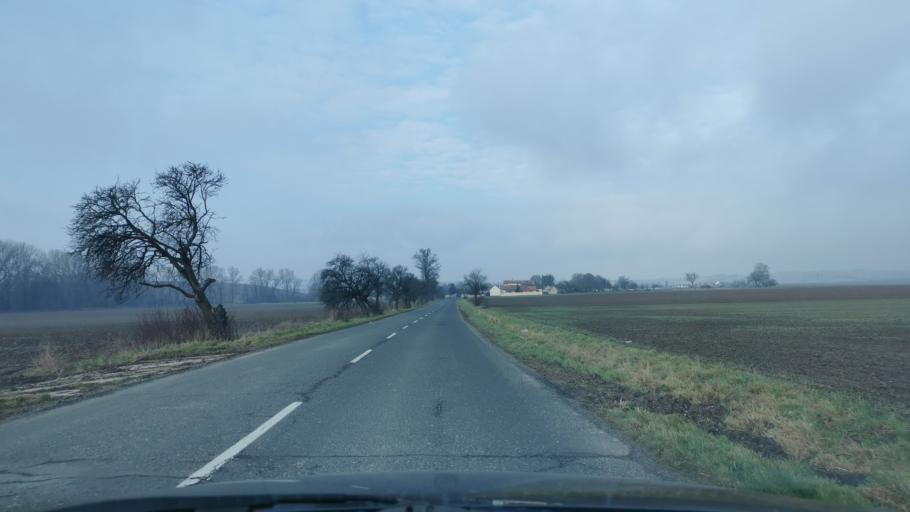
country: SK
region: Trnavsky
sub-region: Okres Senica
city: Senica
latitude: 48.6993
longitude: 17.3462
